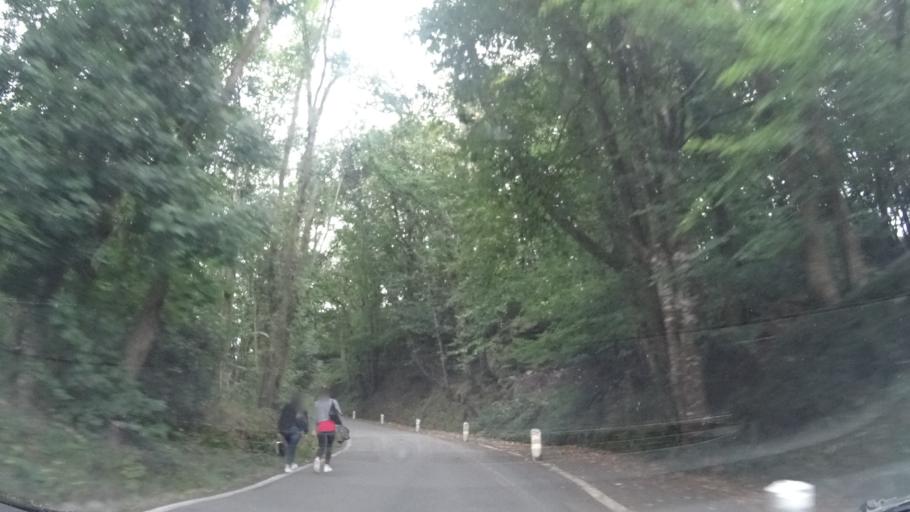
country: FR
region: Brittany
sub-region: Departement du Finistere
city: Le Relecq-Kerhuon
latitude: 48.3883
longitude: -4.3782
